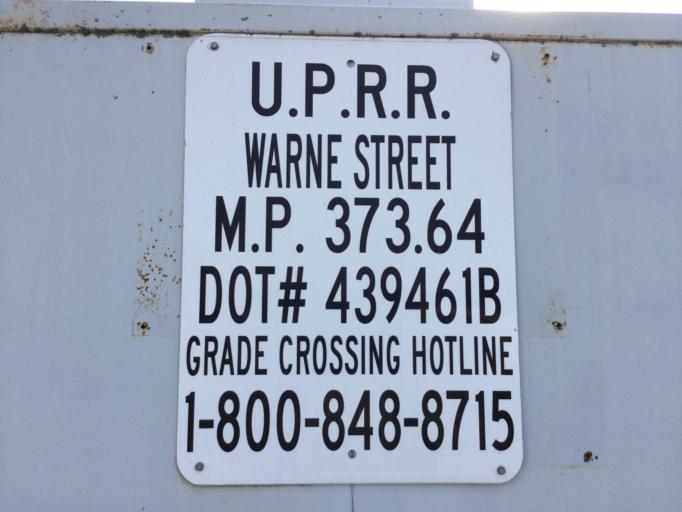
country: US
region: Kansas
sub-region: Coffey County
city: Burlington
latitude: 38.1807
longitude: -95.4886
